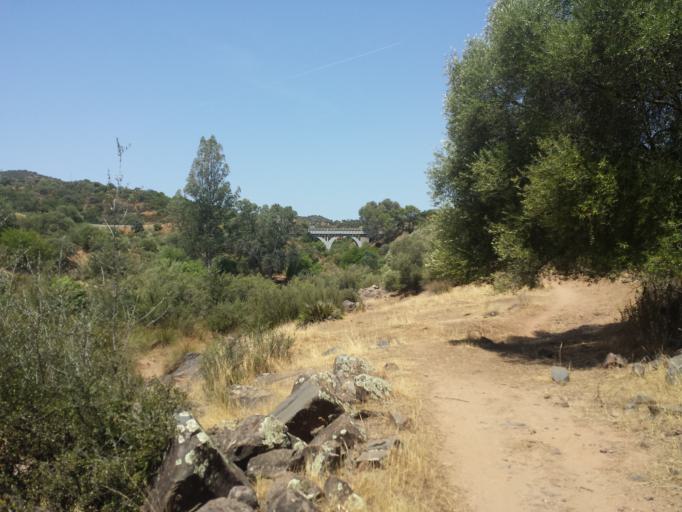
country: ES
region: Andalusia
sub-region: Provincia de Sevilla
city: Castilblanco de los Arroyos
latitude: 37.7157
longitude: -5.8805
